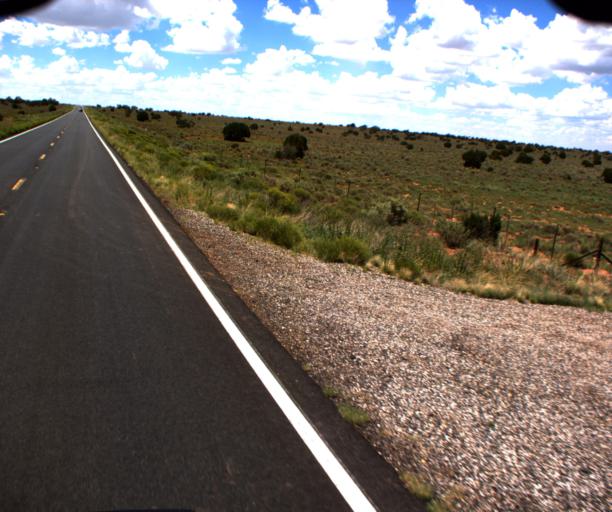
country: US
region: Arizona
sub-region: Coconino County
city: Parks
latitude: 35.6164
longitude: -112.0855
